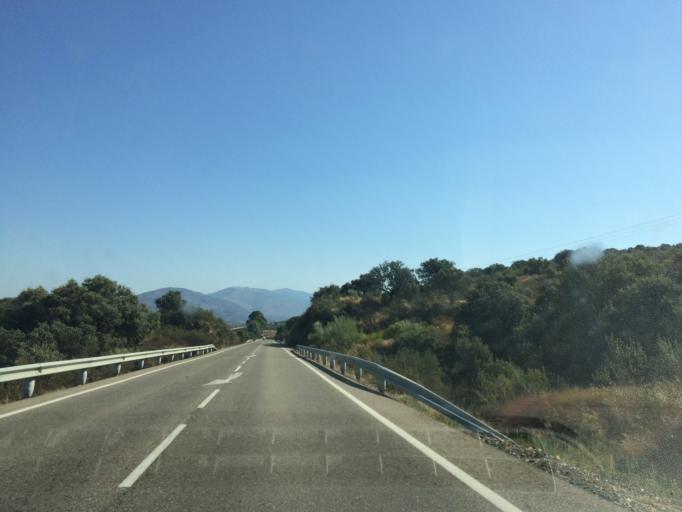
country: ES
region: Extremadura
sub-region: Provincia de Caceres
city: Plasencia
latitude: 39.9957
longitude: -6.0988
